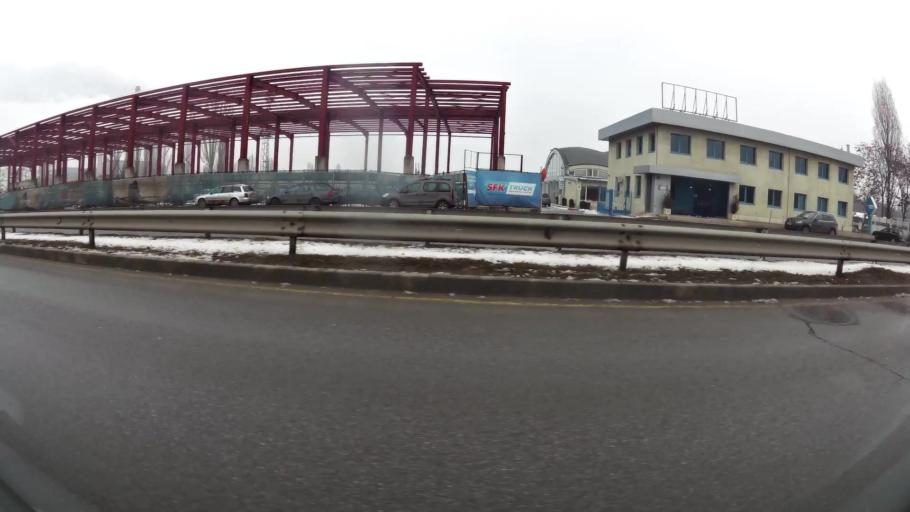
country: BG
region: Sofia-Capital
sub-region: Stolichna Obshtina
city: Sofia
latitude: 42.7153
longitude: 23.3246
